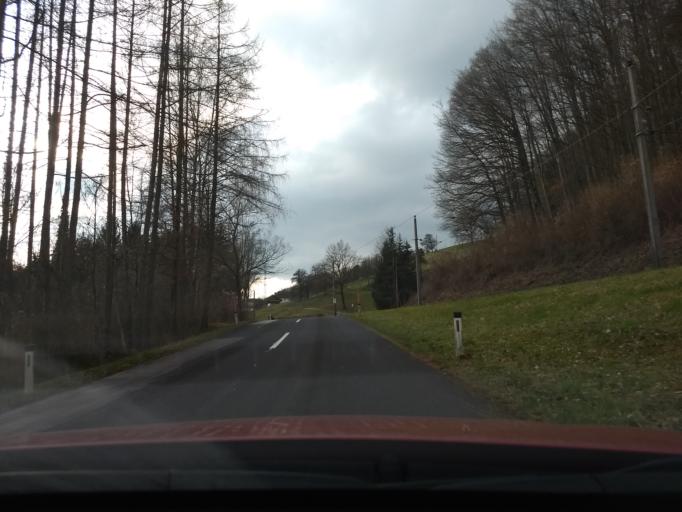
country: AT
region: Upper Austria
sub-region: Politischer Bezirk Steyr-Land
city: Garsten
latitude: 48.0015
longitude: 14.3975
